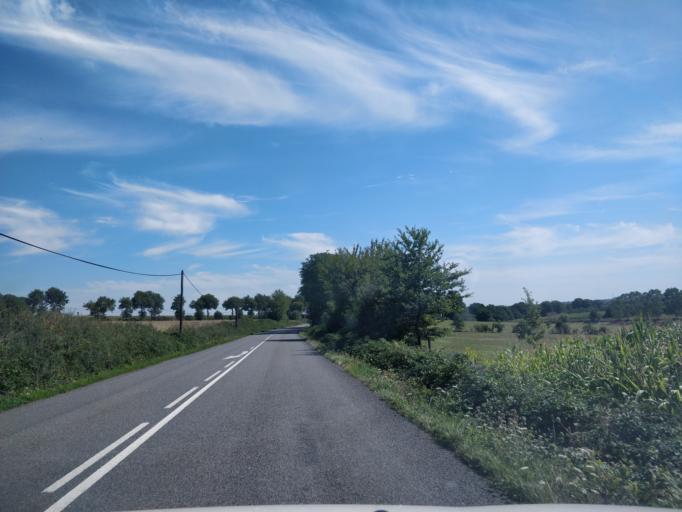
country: FR
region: Brittany
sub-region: Departement d'Ille-et-Vilaine
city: Grand-Fougeray
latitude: 47.6845
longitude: -1.7499
